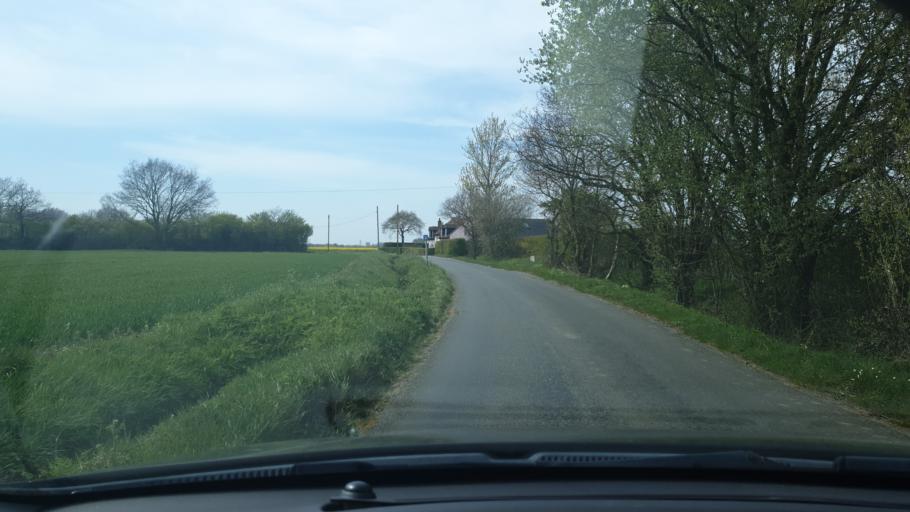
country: GB
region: England
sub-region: Essex
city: Mistley
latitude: 51.8979
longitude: 1.1036
